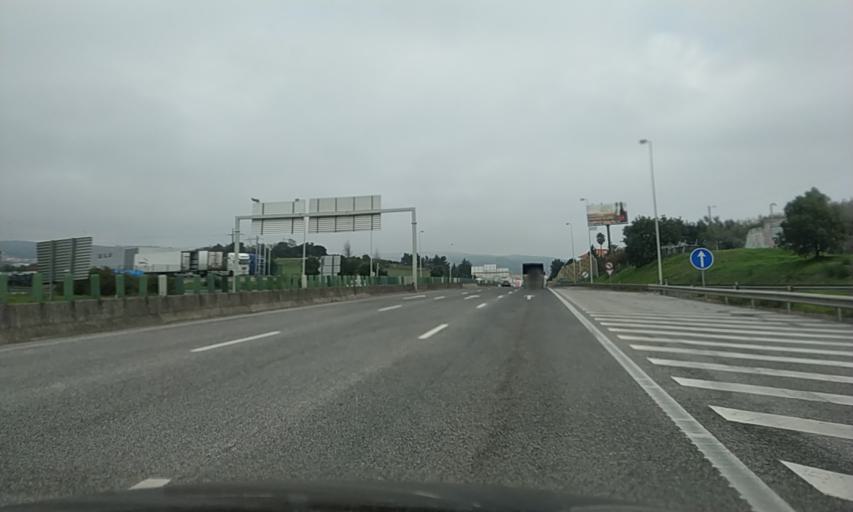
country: PT
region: Lisbon
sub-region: Vila Franca de Xira
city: Vialonga
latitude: 38.8944
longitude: -9.0483
